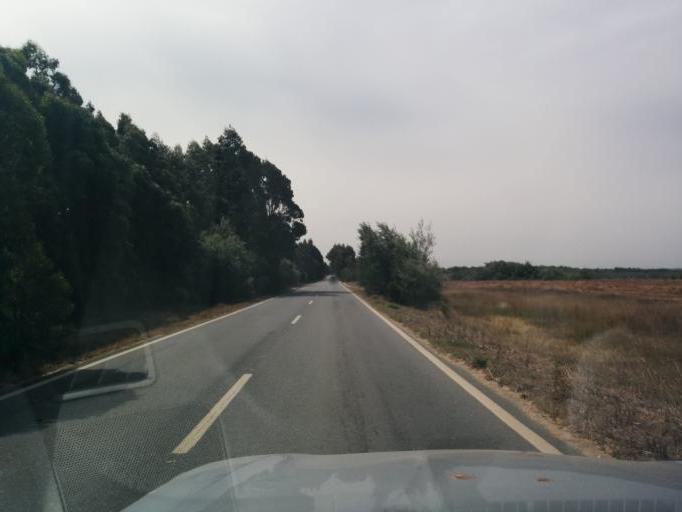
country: PT
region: Beja
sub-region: Odemira
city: Vila Nova de Milfontes
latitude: 37.6863
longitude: -8.7652
